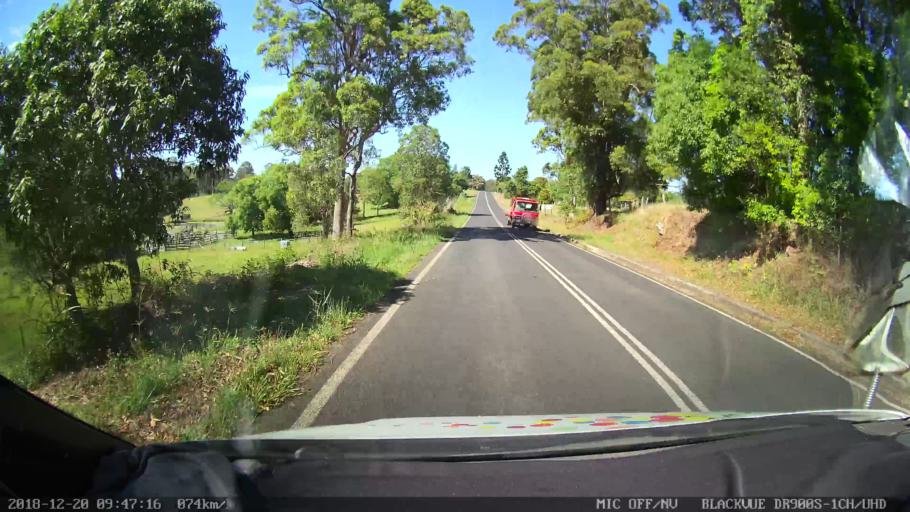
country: AU
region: New South Wales
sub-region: Lismore Municipality
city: Lismore
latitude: -28.7615
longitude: 153.2985
